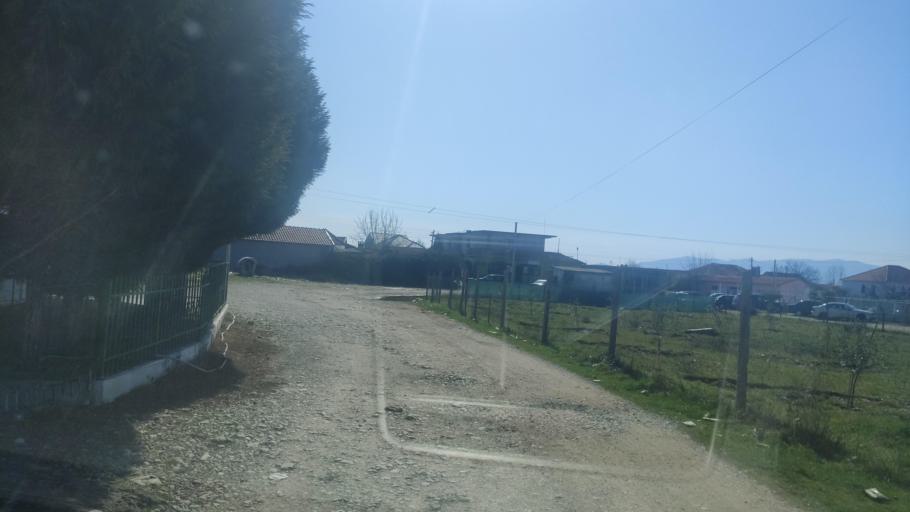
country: AL
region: Shkoder
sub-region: Rrethi i Malesia e Madhe
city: Grude-Fushe
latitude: 42.1698
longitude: 19.4825
